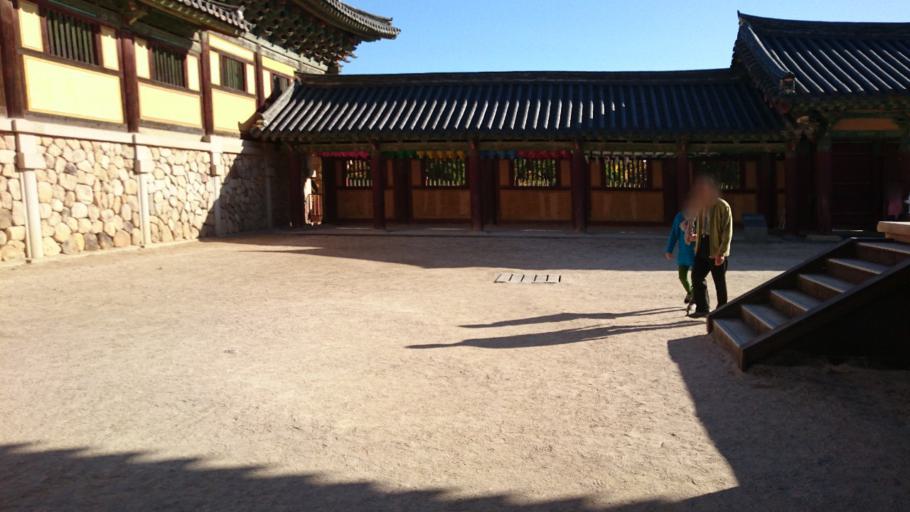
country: KR
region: Gyeongsangbuk-do
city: Kyonju
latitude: 35.7900
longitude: 129.3317
